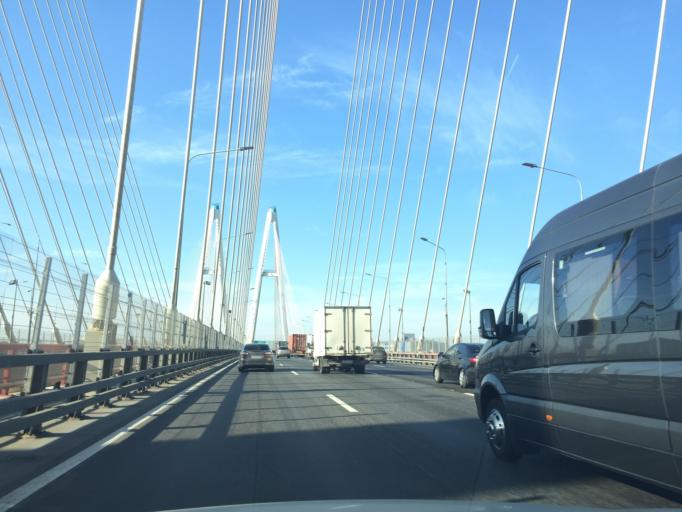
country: RU
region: Leningrad
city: Rybatskoye
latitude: 59.8520
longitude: 30.4875
